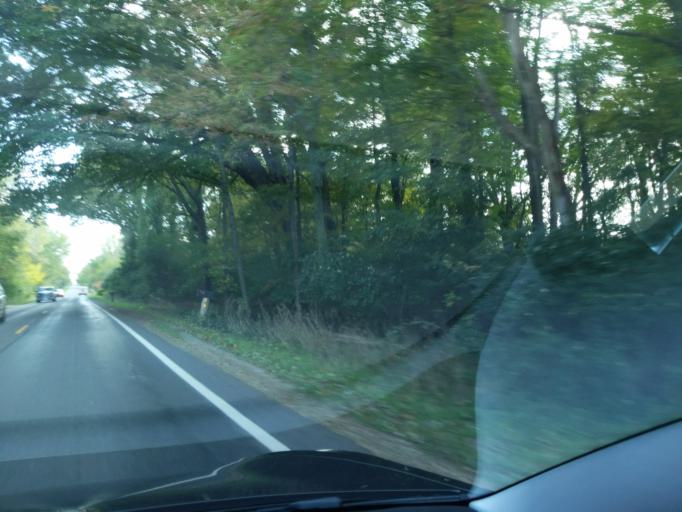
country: US
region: Michigan
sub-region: Jackson County
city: Jackson
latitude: 42.3173
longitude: -84.4628
